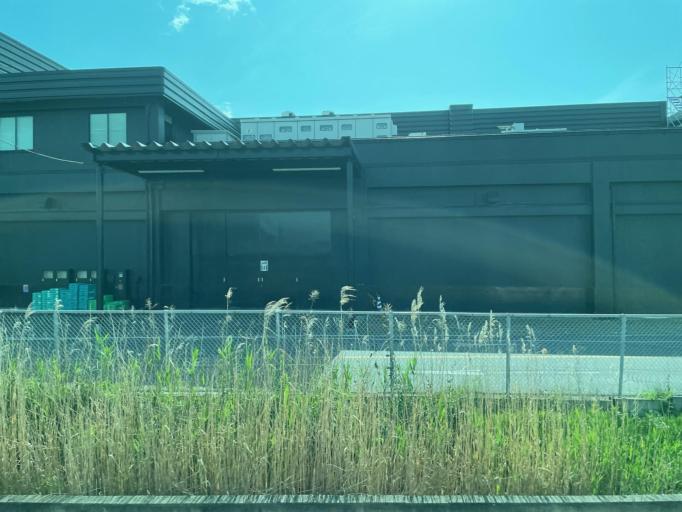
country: JP
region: Saitama
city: Satte
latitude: 36.0615
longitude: 139.7138
